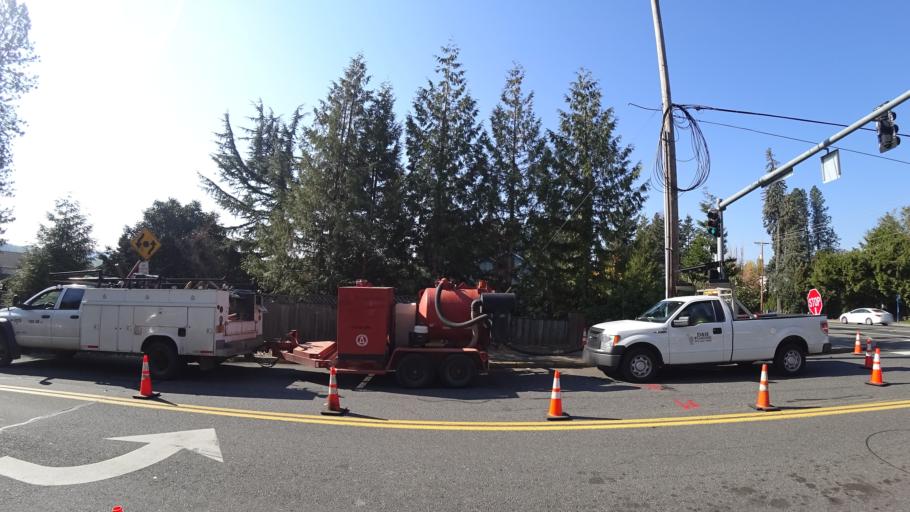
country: US
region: Oregon
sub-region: Multnomah County
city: Gresham
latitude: 45.4968
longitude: -122.4549
